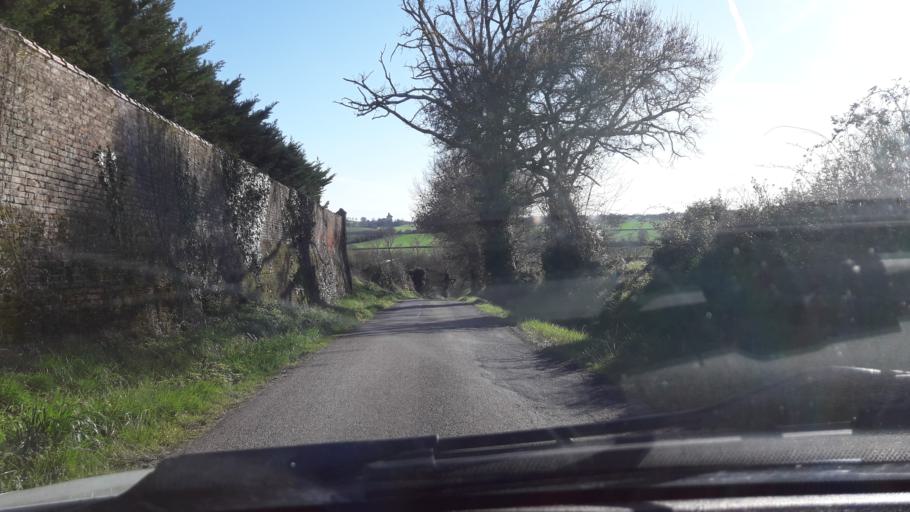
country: FR
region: Midi-Pyrenees
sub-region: Departement du Gers
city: Gimont
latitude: 43.6011
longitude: 0.9780
